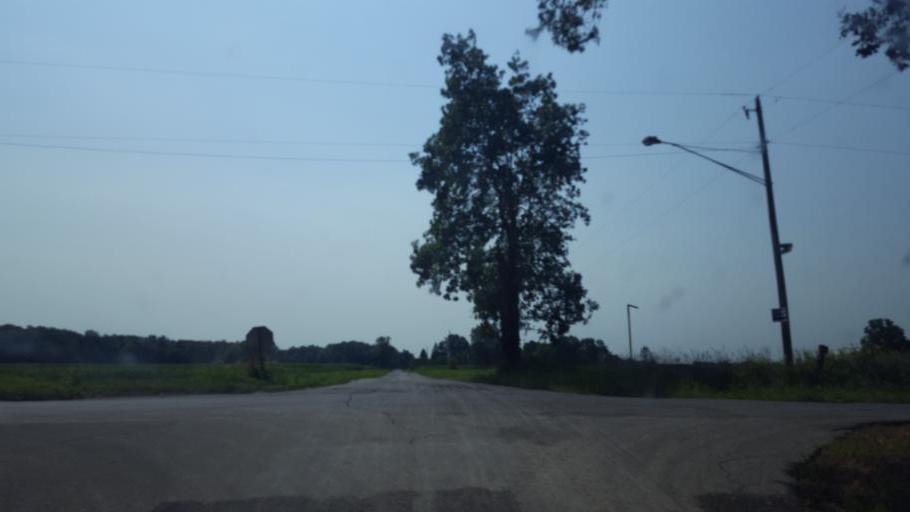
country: US
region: Ohio
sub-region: Ashtabula County
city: Orwell
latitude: 41.4892
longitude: -80.8778
